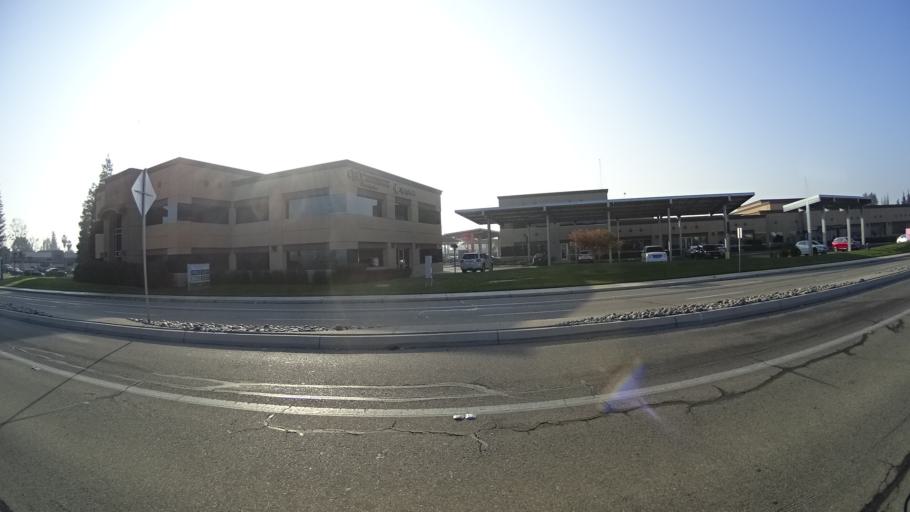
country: US
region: California
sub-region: Kern County
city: Greenacres
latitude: 35.3623
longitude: -119.0741
